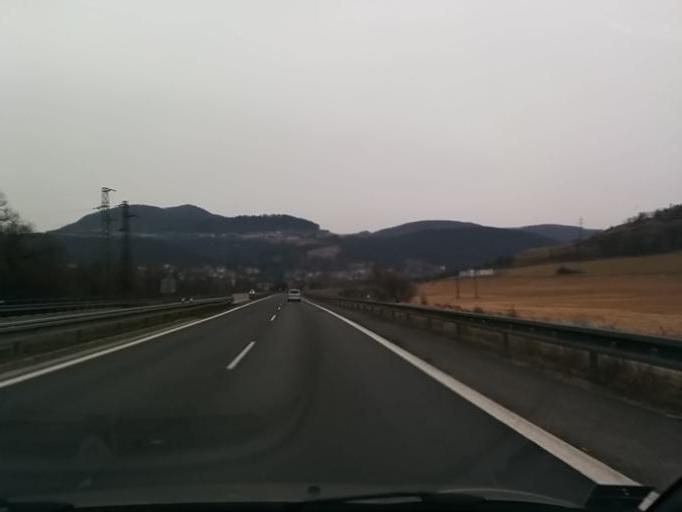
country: SK
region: Banskobystricky
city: Ziar nad Hronom
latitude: 48.5831
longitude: 18.9443
